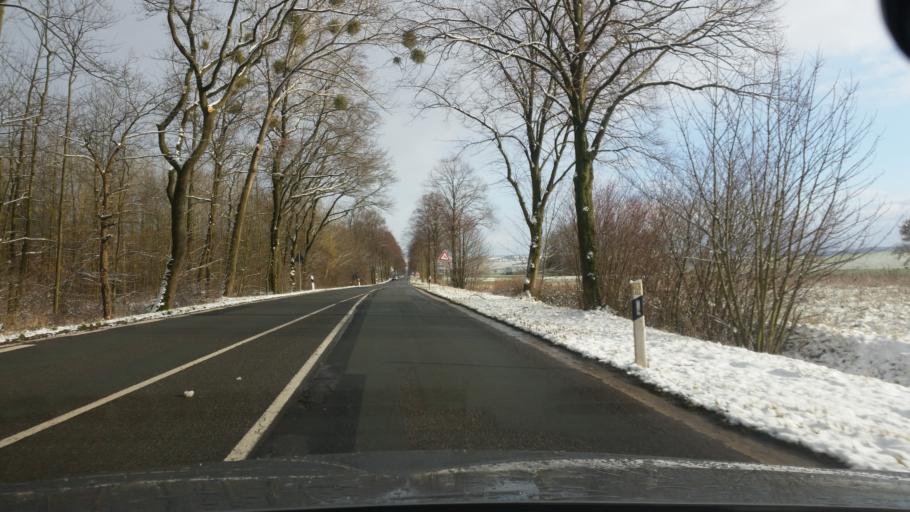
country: DE
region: Lower Saxony
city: Bad Munder am Deister
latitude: 52.1480
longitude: 9.4168
